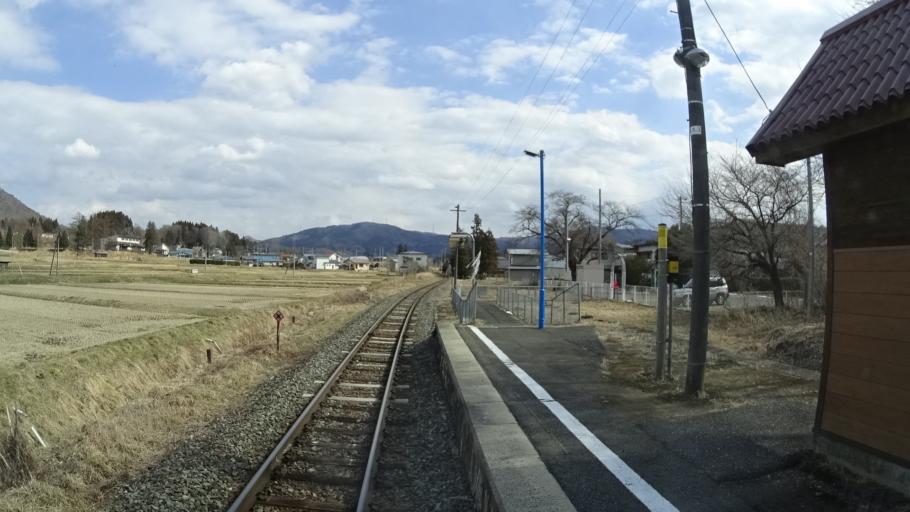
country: JP
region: Iwate
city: Hanamaki
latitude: 39.3664
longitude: 141.2581
